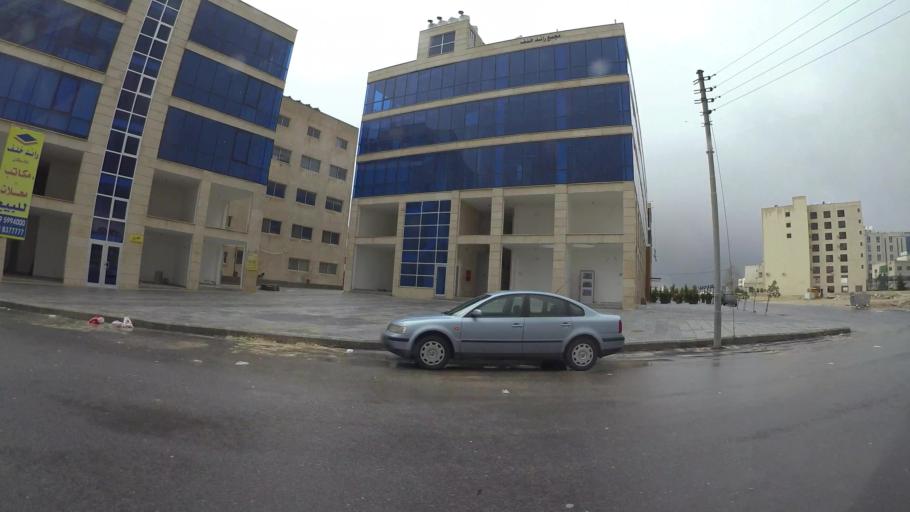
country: JO
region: Amman
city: Wadi as Sir
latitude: 31.9581
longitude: 35.8562
